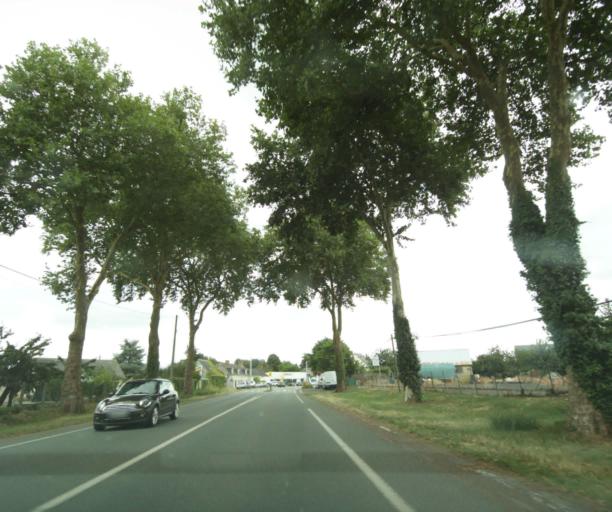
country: FR
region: Pays de la Loire
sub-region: Departement de Maine-et-Loire
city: Pellouailles-les-Vignes
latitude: 47.5226
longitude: -0.4337
